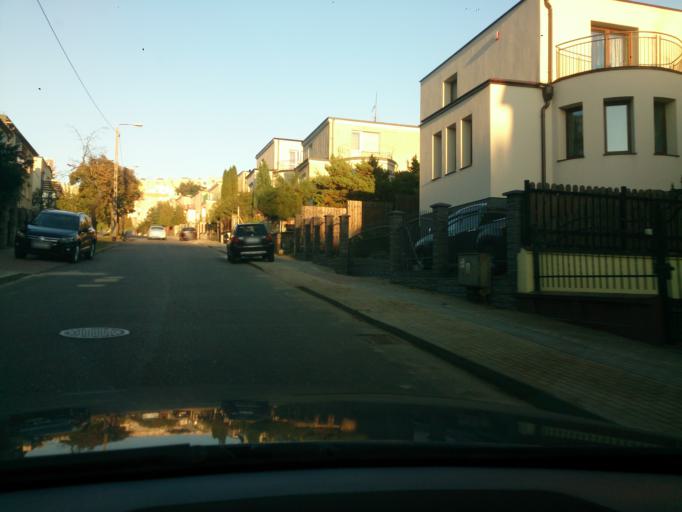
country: PL
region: Pomeranian Voivodeship
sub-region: Gdynia
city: Gdynia
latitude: 54.4918
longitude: 18.5470
